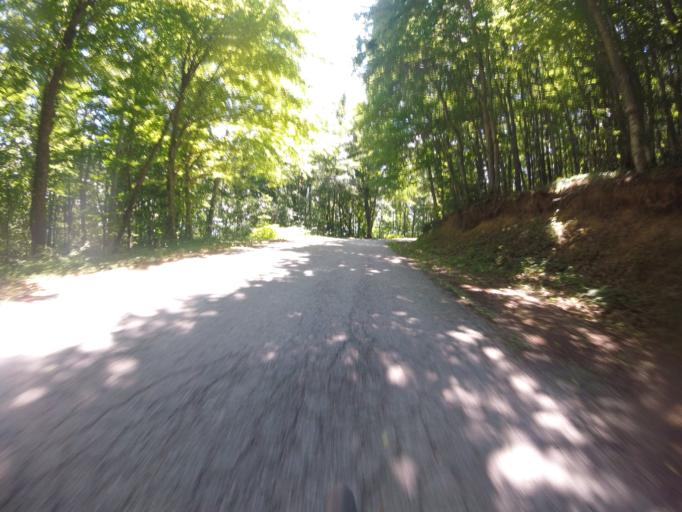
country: SI
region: Metlika
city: Metlika
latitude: 45.7146
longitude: 15.3849
